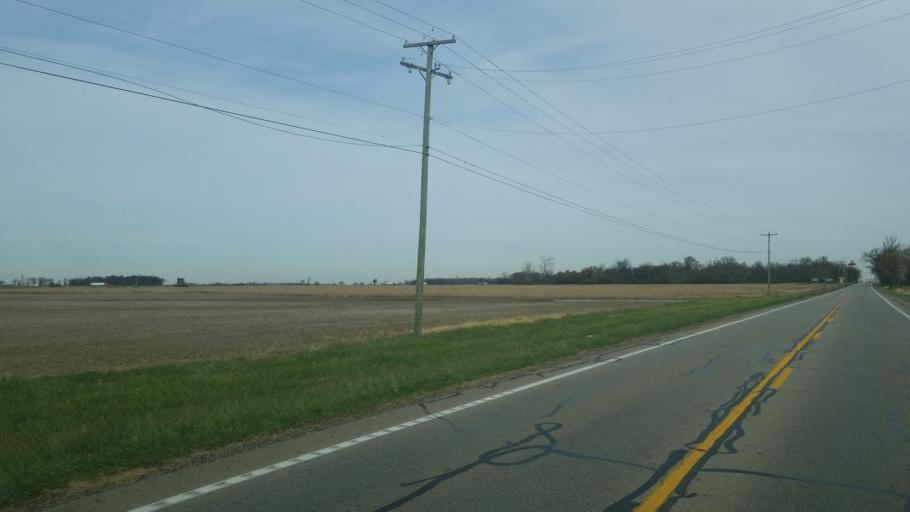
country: US
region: Ohio
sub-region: Madison County
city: London
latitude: 39.9423
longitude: -83.3912
